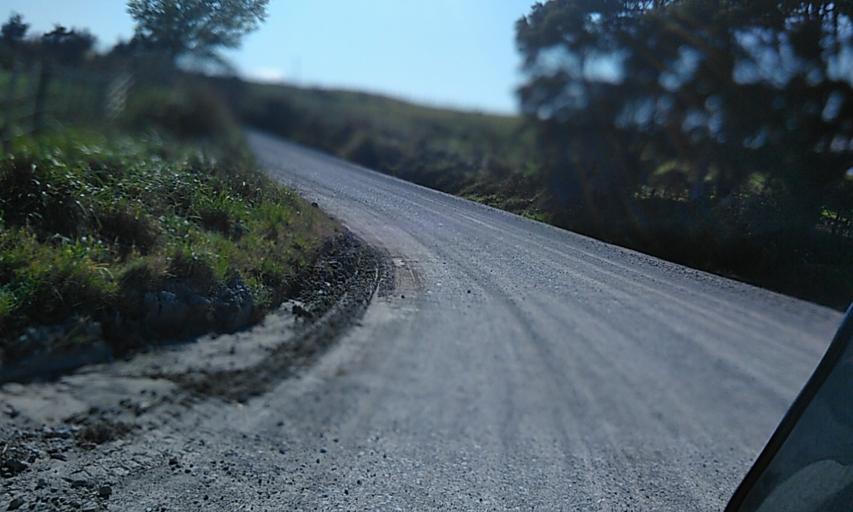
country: NZ
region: Gisborne
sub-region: Gisborne District
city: Gisborne
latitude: -38.4943
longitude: 178.0591
